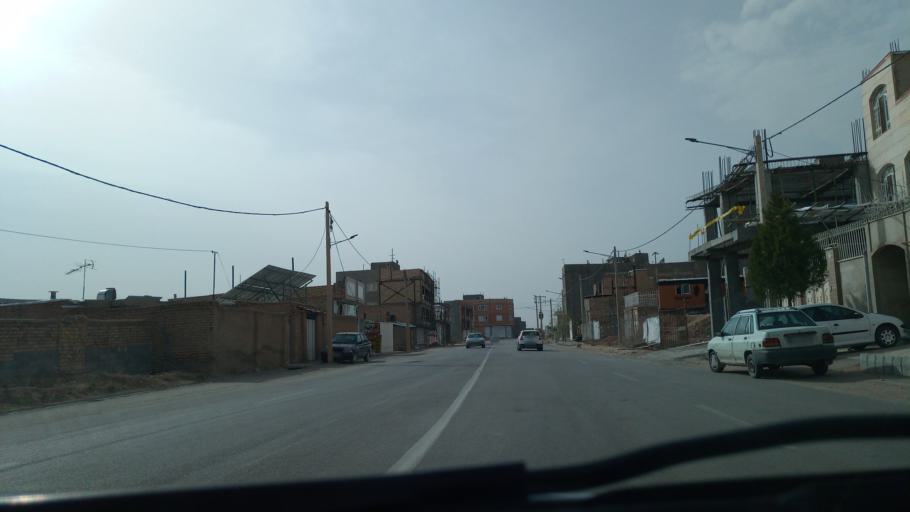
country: IR
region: Khorasan-e Shomali
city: Esfarayen
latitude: 37.0828
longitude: 57.5081
